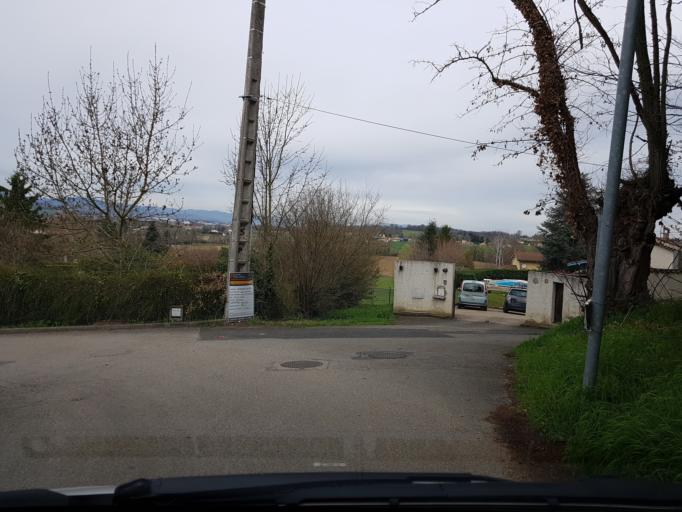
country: FR
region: Rhone-Alpes
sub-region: Departement de l'Ain
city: Trevoux
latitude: 45.9498
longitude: 4.7639
